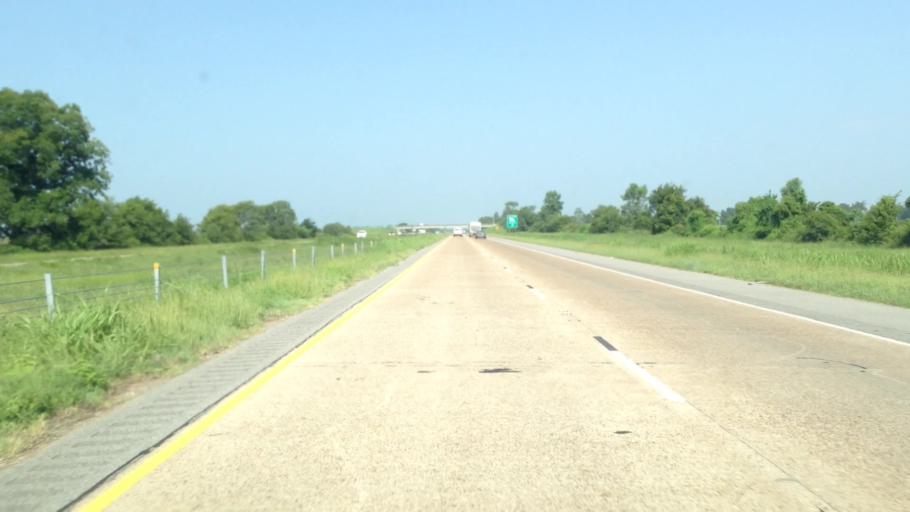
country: US
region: Mississippi
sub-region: Warren County
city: Vicksburg
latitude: 32.3287
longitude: -91.0154
